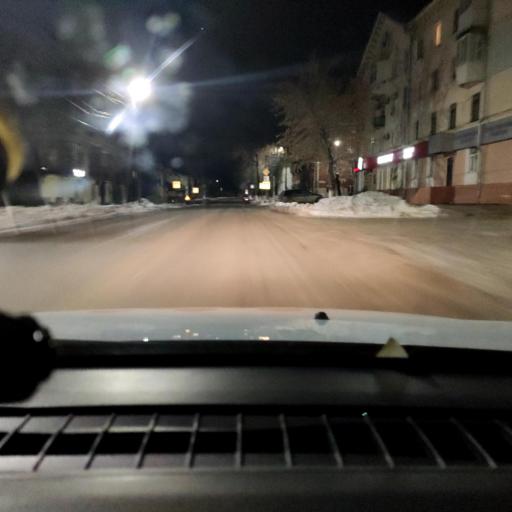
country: RU
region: Samara
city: Novokuybyshevsk
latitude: 53.1007
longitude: 49.9518
